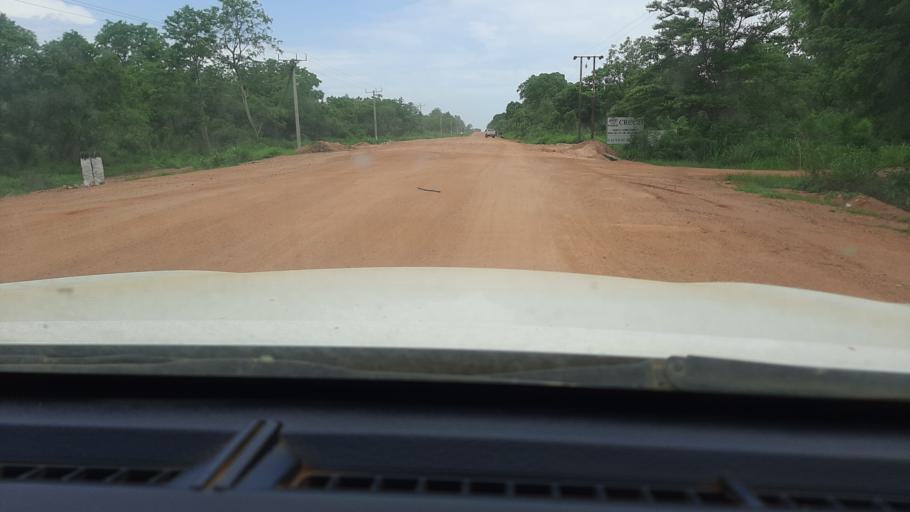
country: ET
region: Gambela
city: Gambela
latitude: 8.1414
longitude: 34.5771
